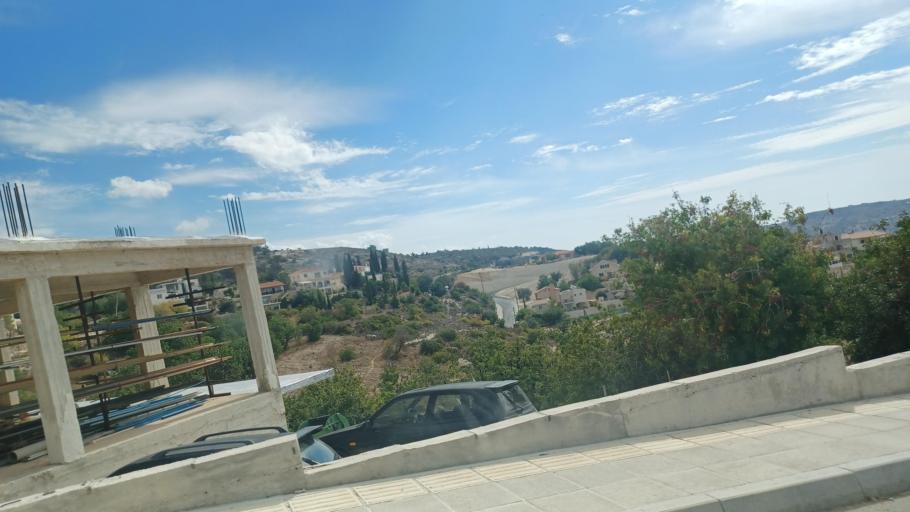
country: CY
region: Pafos
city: Mesogi
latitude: 34.8116
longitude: 32.4640
